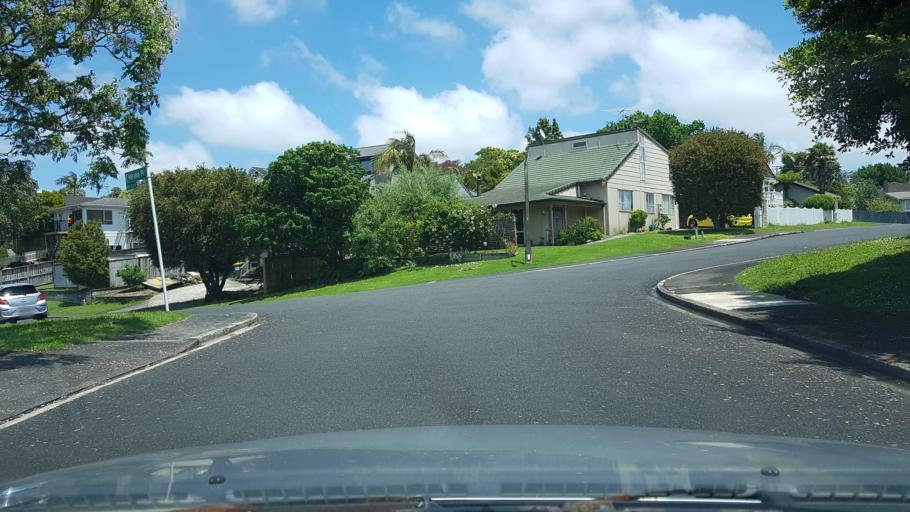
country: NZ
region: Auckland
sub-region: Auckland
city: North Shore
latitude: -36.8070
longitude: 174.7167
